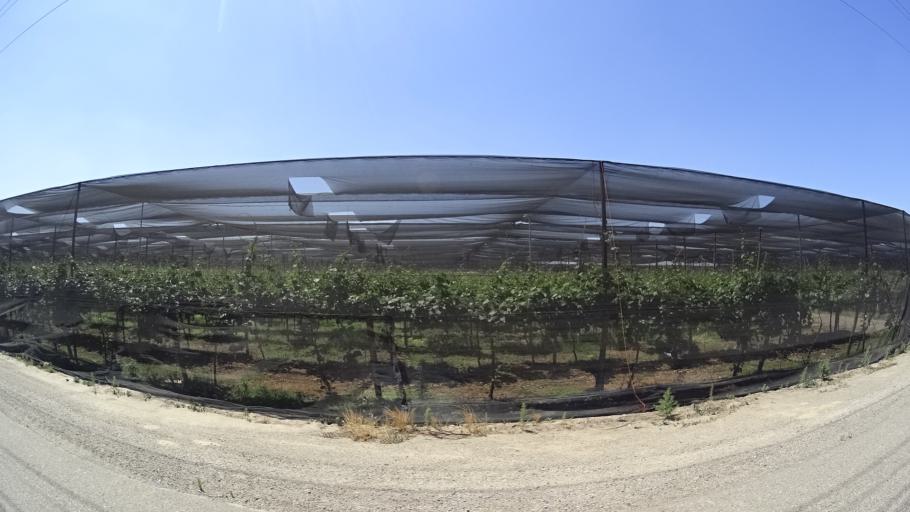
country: US
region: California
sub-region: Fresno County
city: Kingsburg
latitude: 36.4888
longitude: -119.5802
